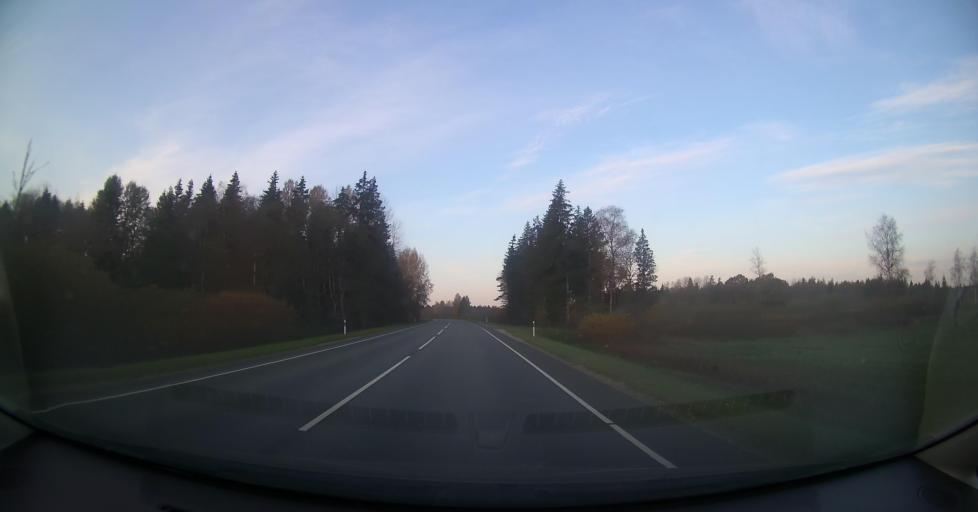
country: EE
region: Harju
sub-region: Nissi vald
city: Riisipere
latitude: 59.1191
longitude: 24.2805
